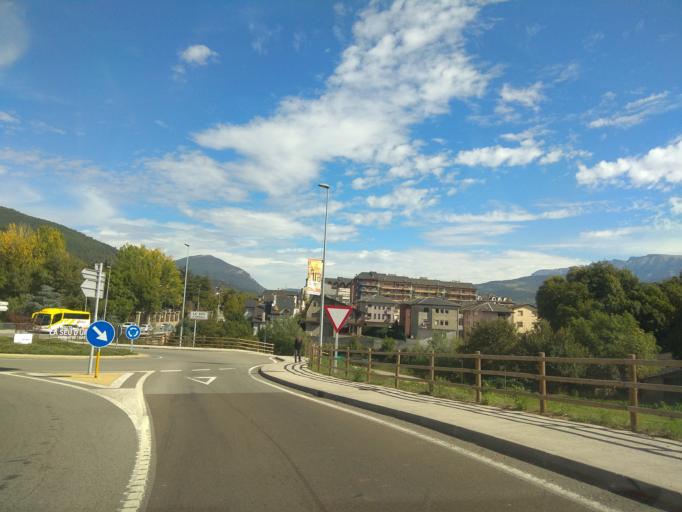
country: ES
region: Catalonia
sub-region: Provincia de Lleida
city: la Seu d'Urgell
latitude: 42.3602
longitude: 1.4538
